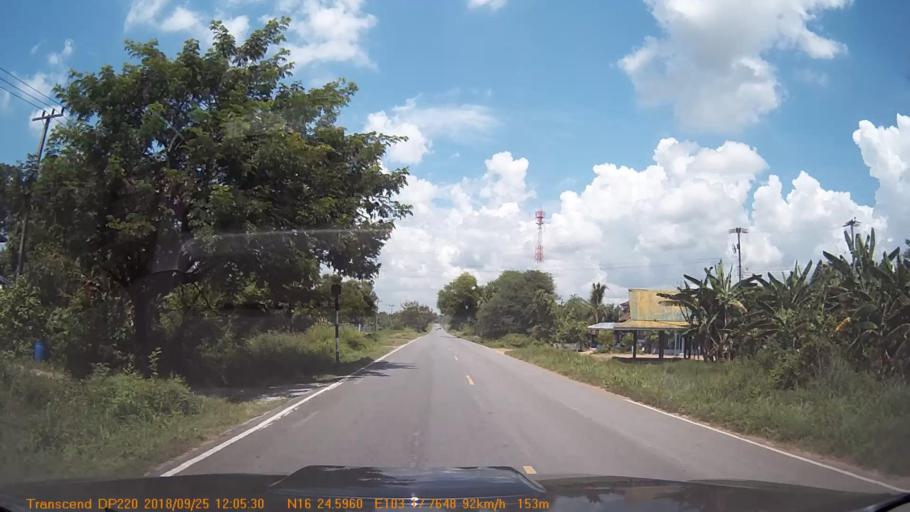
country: TH
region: Kalasin
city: Yang Talat
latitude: 16.4099
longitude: 103.2961
